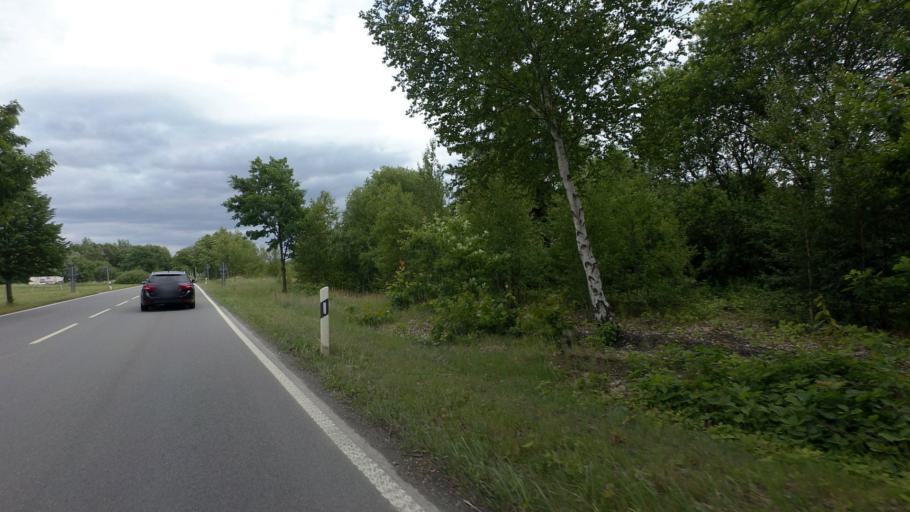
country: DE
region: Saxony
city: Ossling
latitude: 51.4433
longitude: 14.1364
